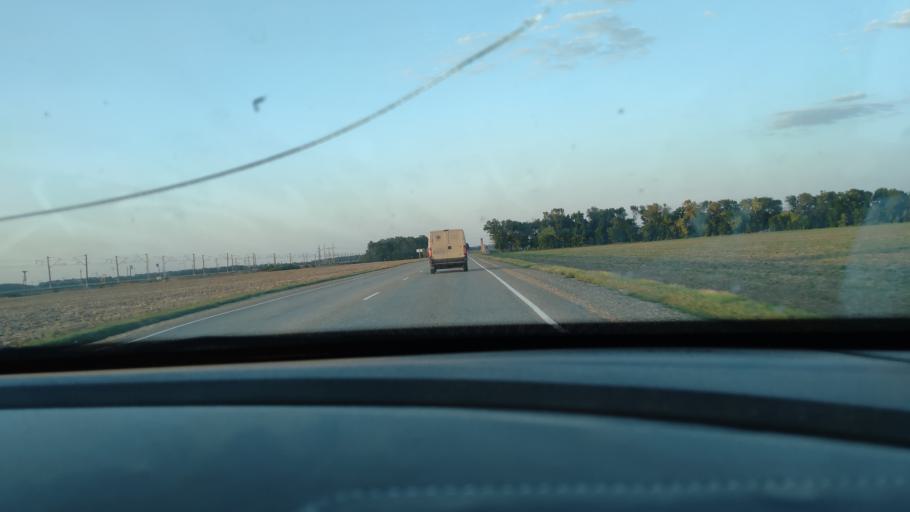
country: RU
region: Krasnodarskiy
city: Novominskaya
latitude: 46.3916
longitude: 38.9904
